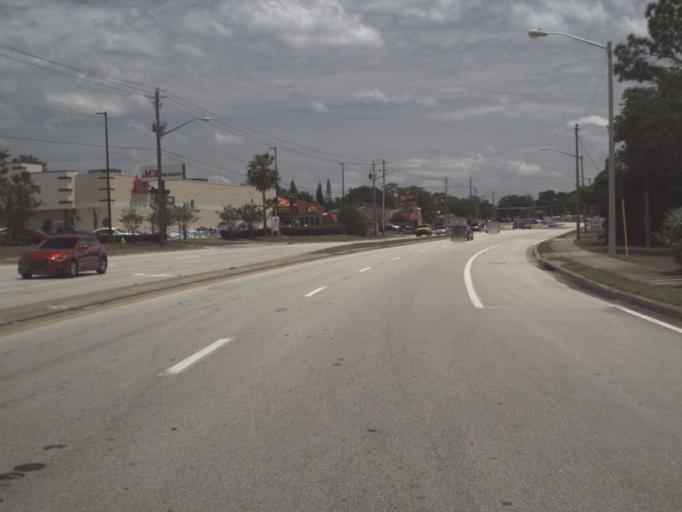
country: US
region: Florida
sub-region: Brevard County
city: Titusville
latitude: 28.6184
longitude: -80.8426
